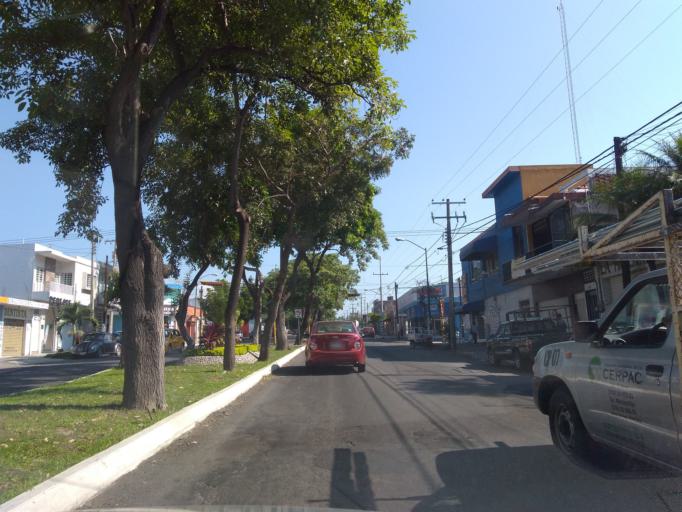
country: MX
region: Colima
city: Colima
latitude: 19.2497
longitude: -103.7324
